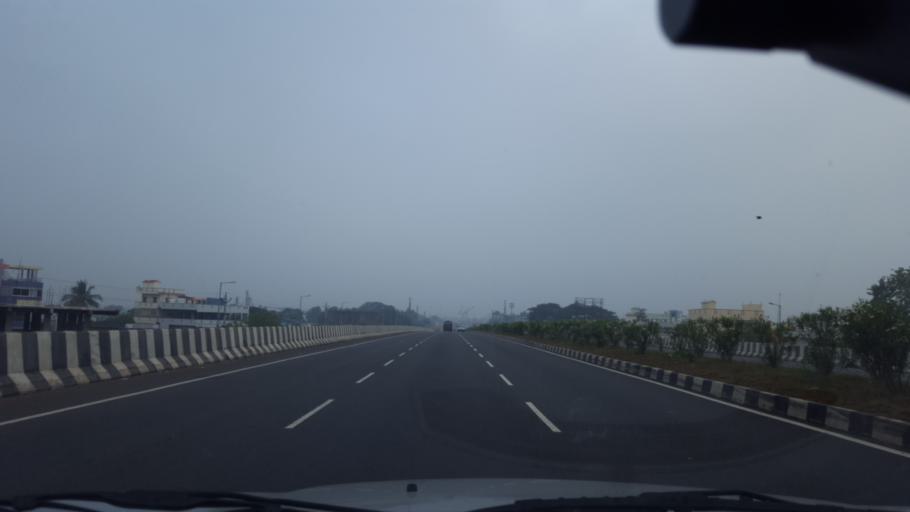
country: IN
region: Andhra Pradesh
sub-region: Prakasam
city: Ongole
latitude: 15.6206
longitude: 80.0216
